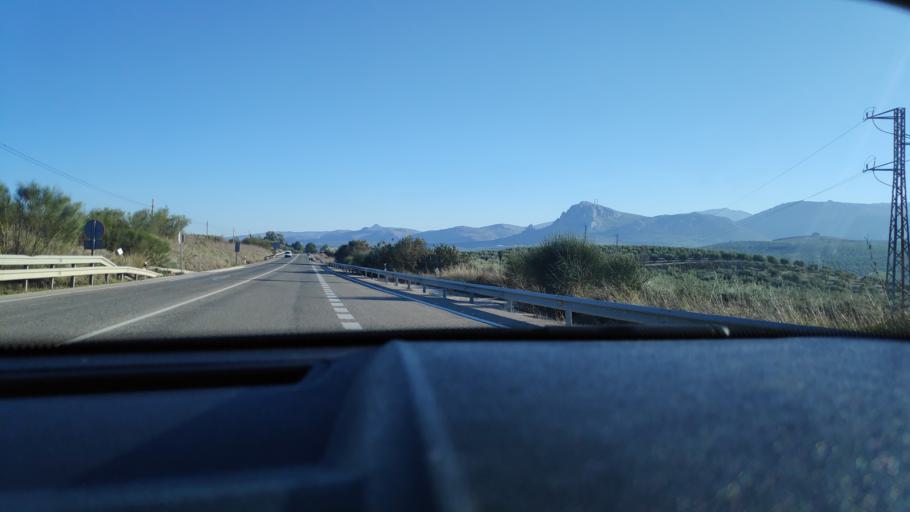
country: ES
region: Andalusia
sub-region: Province of Cordoba
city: Baena
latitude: 37.5930
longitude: -4.2993
